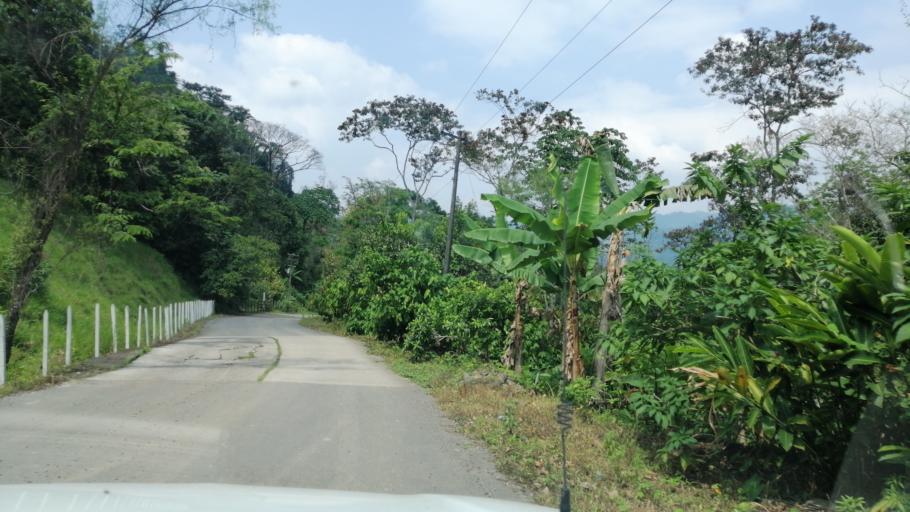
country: MX
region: Chiapas
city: Ostuacan
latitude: 17.3913
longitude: -93.3304
